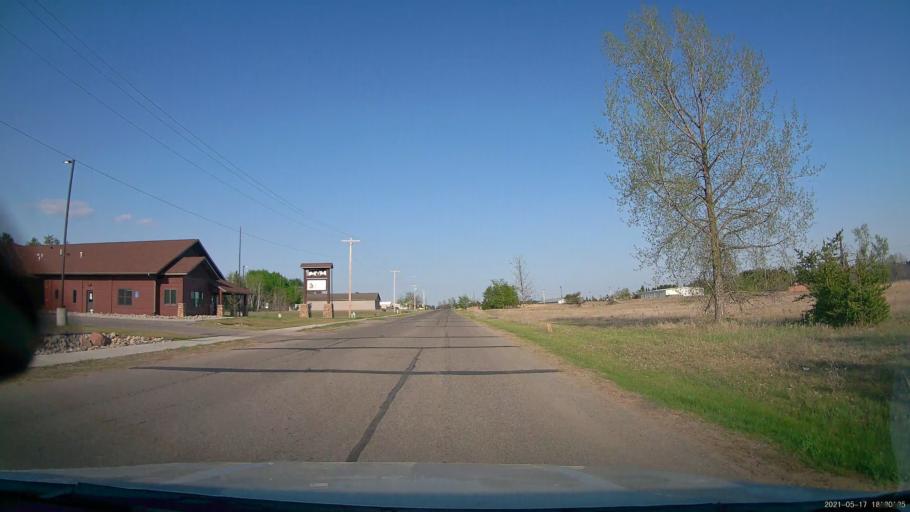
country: US
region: Minnesota
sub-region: Hubbard County
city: Park Rapids
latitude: 46.9248
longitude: -95.0401
